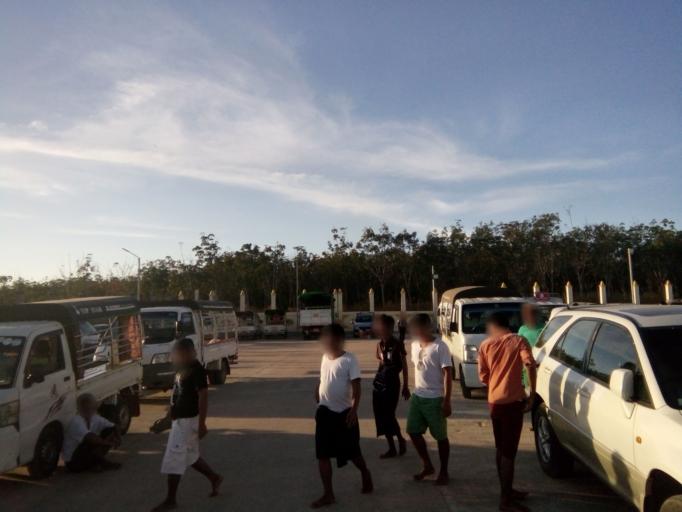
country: MM
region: Bago
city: Thanatpin
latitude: 17.2736
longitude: 96.2351
